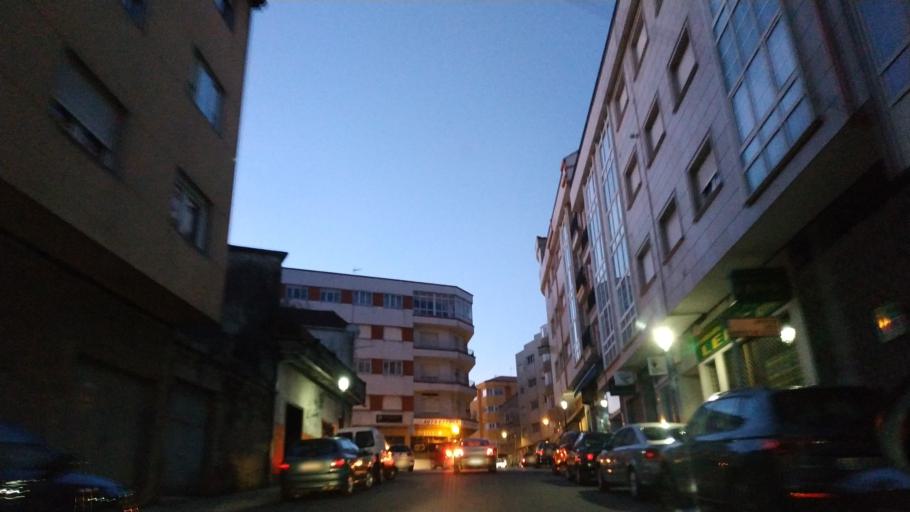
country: ES
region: Galicia
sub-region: Provincia da Coruna
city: Negreira
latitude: 42.9099
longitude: -8.7350
